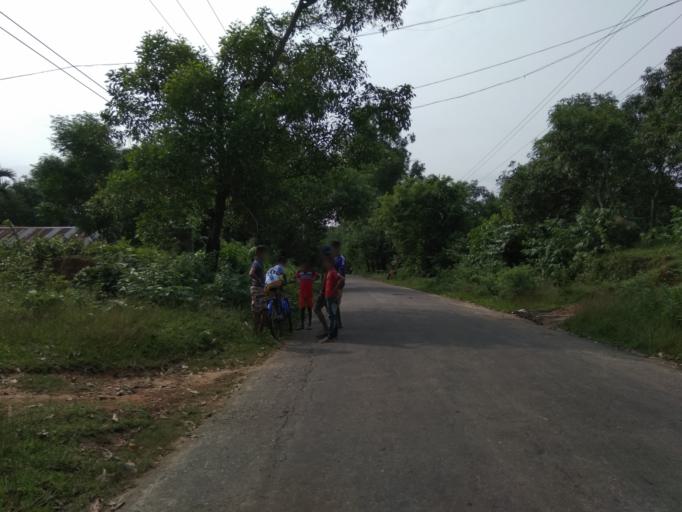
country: BD
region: Chittagong
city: Khagrachhari
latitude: 23.0316
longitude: 92.0104
